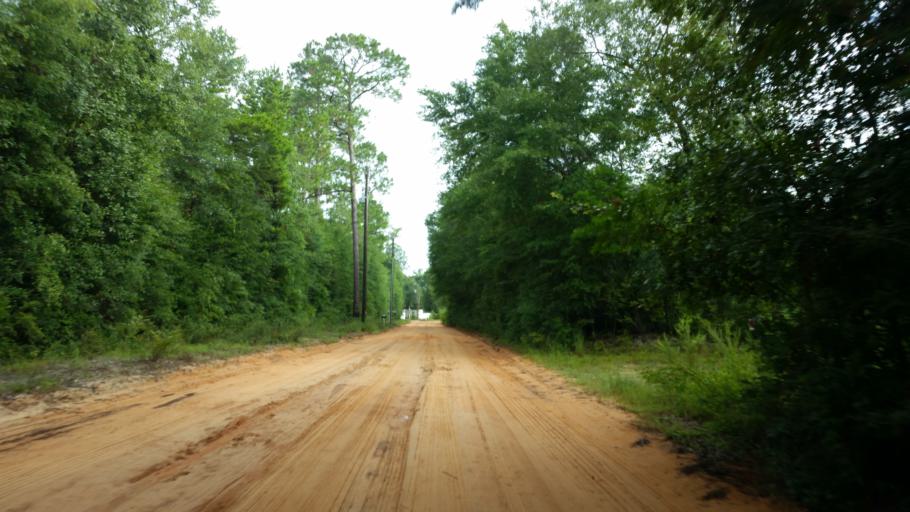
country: US
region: Florida
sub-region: Okaloosa County
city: Crestview
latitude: 30.6711
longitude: -86.7567
